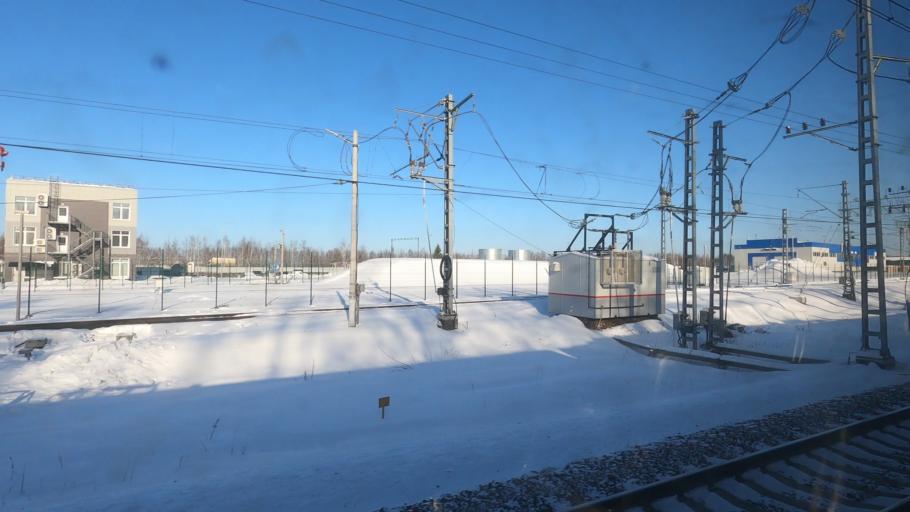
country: RU
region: Moskovskaya
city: Elektrougli
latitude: 55.7238
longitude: 38.2265
